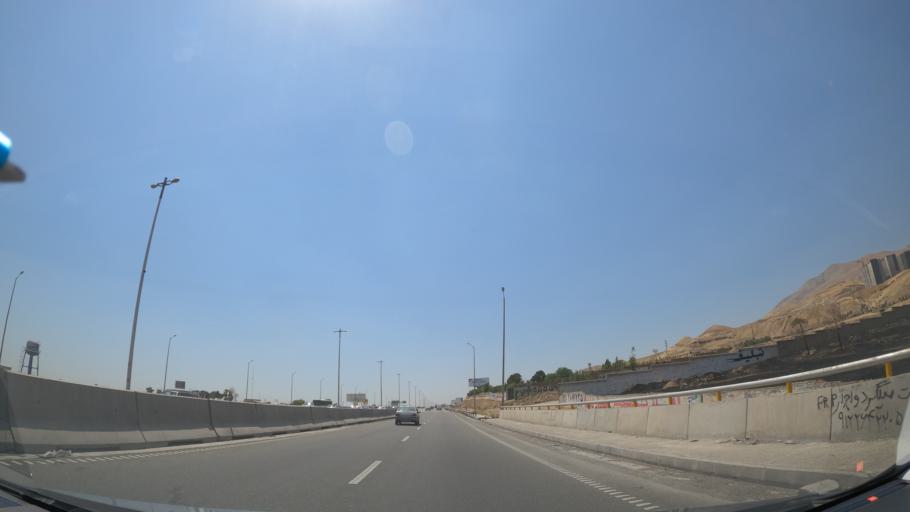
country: IR
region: Tehran
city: Shahr-e Qods
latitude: 35.7422
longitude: 51.1152
